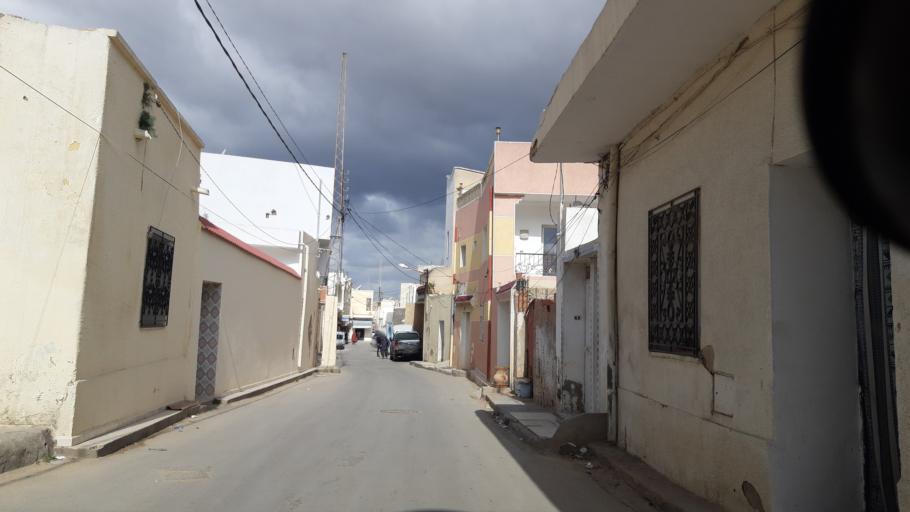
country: TN
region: Susah
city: Akouda
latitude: 35.8711
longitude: 10.5292
